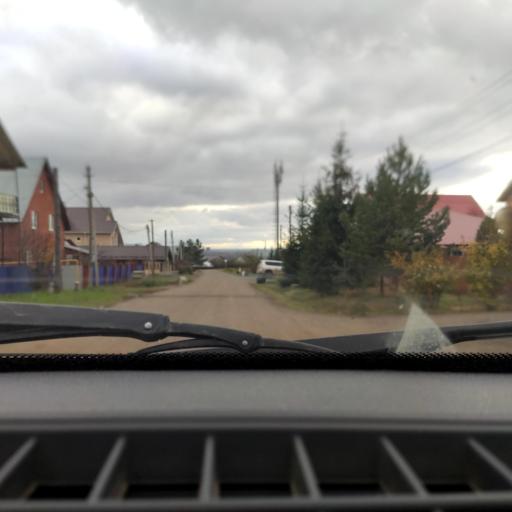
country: RU
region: Bashkortostan
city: Mikhaylovka
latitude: 54.8162
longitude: 55.8903
